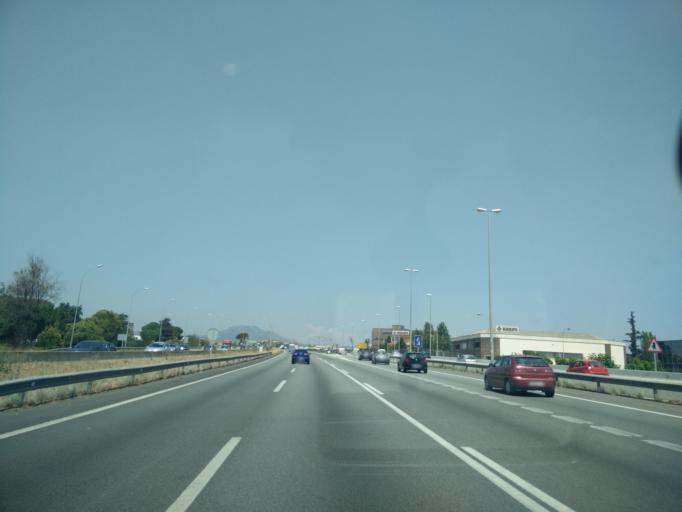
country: ES
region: Catalonia
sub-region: Provincia de Barcelona
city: Sant Quirze del Valles
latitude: 41.5255
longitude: 2.0959
